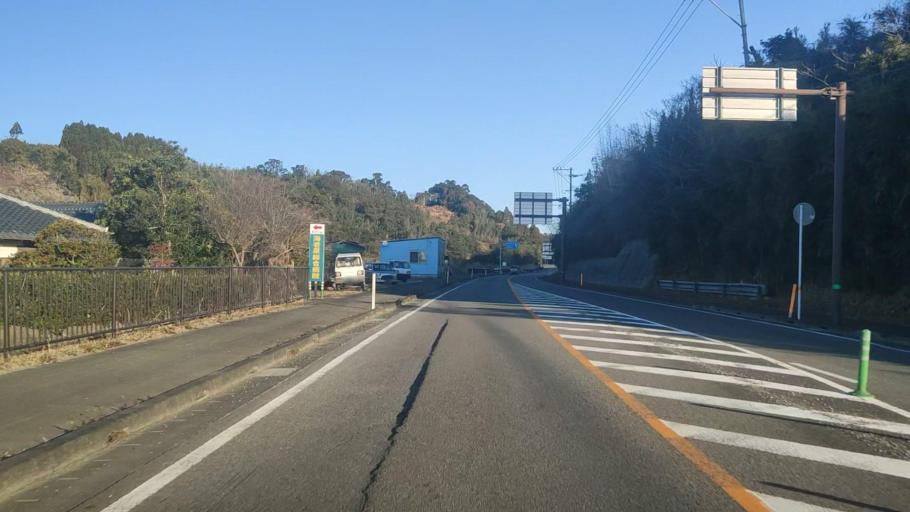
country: JP
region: Miyazaki
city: Takanabe
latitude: 32.1461
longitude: 131.5257
